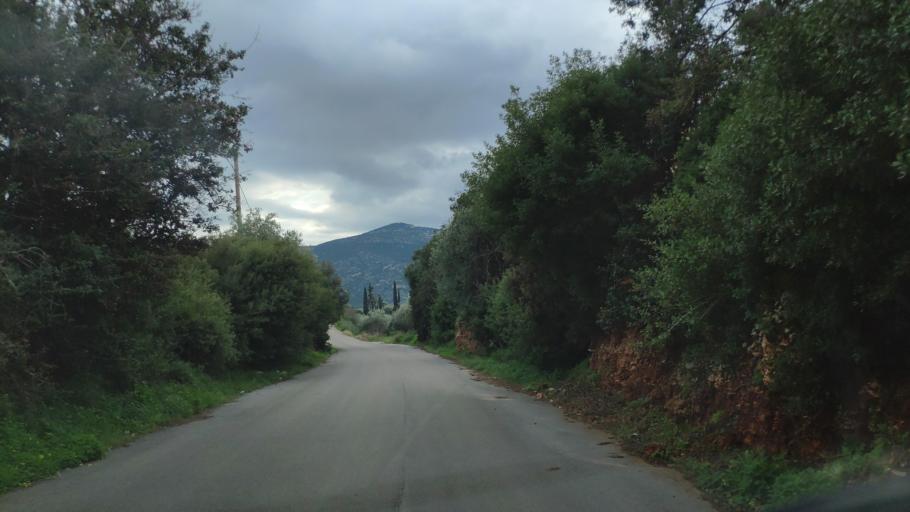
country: GR
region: Peloponnese
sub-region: Nomos Argolidos
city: Nea Kios
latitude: 37.5333
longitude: 22.6965
